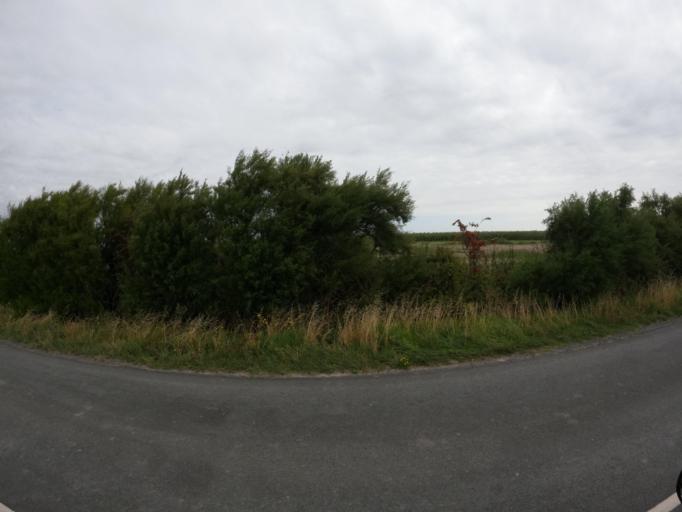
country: FR
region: Poitou-Charentes
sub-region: Departement de la Charente-Maritime
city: Andilly
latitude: 46.3031
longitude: -1.0473
